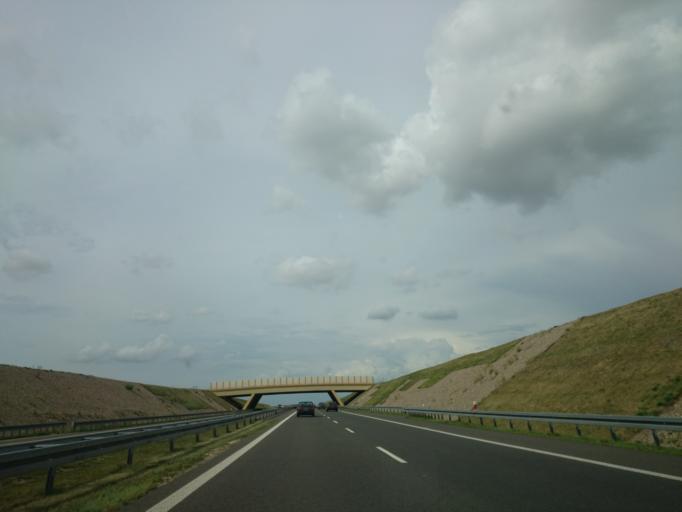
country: PL
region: West Pomeranian Voivodeship
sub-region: Powiat pyrzycki
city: Kozielice
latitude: 53.0654
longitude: 14.8624
